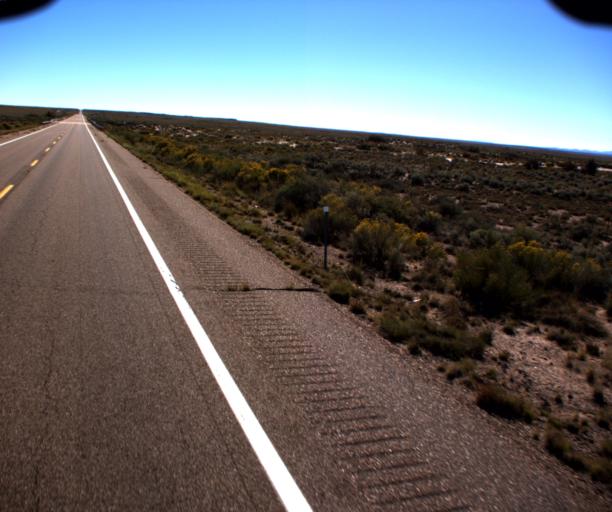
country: US
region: Arizona
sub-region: Navajo County
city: Holbrook
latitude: 34.7895
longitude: -109.8856
